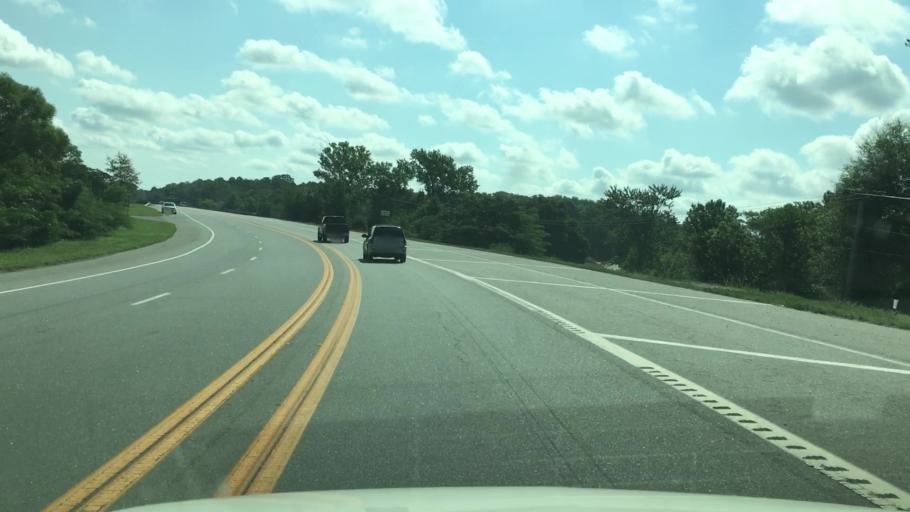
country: US
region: Arkansas
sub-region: Garland County
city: Piney
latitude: 34.5070
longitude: -93.1852
